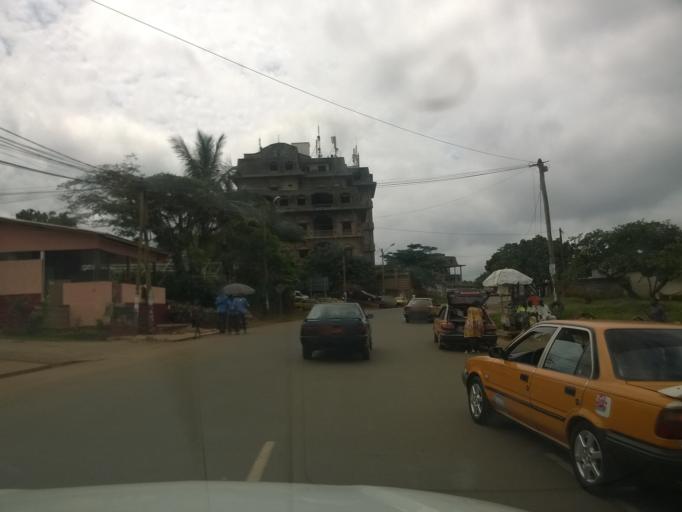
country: CM
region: Centre
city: Yaounde
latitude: 3.8402
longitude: 11.4965
